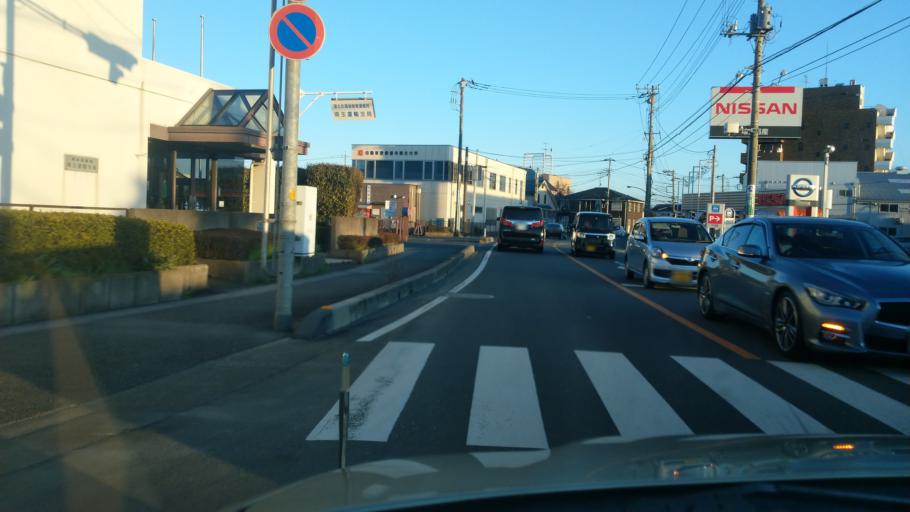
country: JP
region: Saitama
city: Ageoshimo
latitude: 35.9407
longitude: 139.5713
